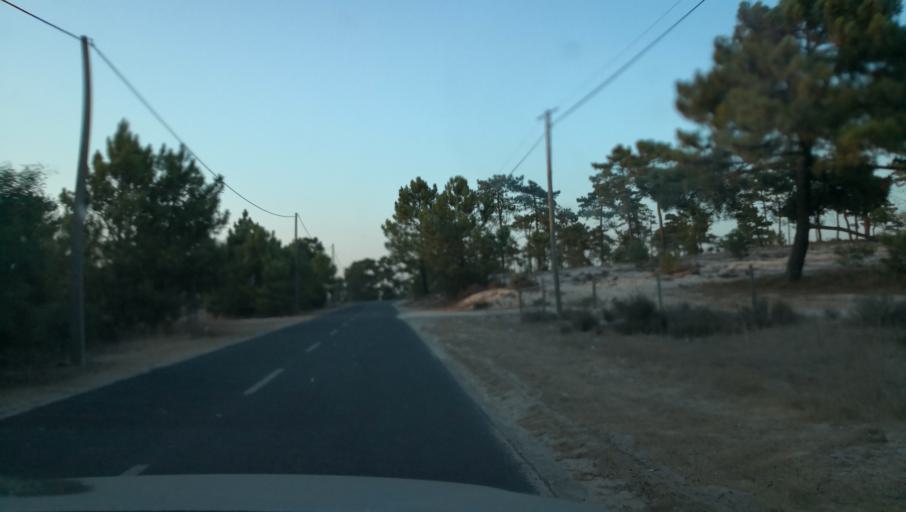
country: PT
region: Setubal
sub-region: Setubal
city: Setubal
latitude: 38.3840
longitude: -8.7828
